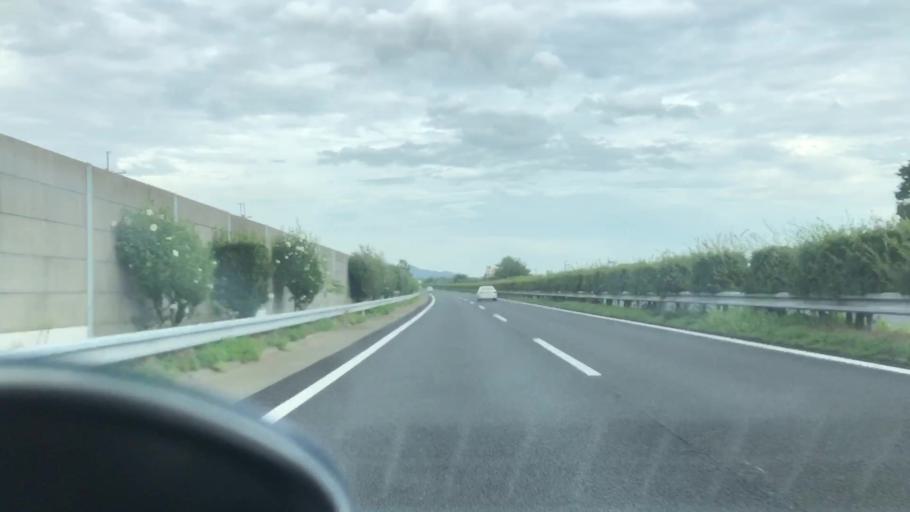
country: JP
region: Hyogo
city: Yashiro
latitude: 34.9288
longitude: 134.9498
